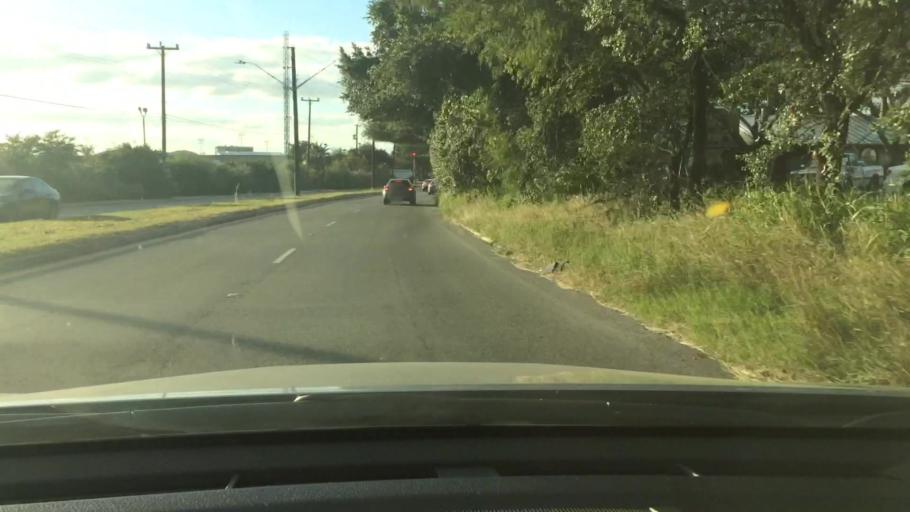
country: US
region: Texas
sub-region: Bexar County
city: Hollywood Park
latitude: 29.5473
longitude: -98.4603
